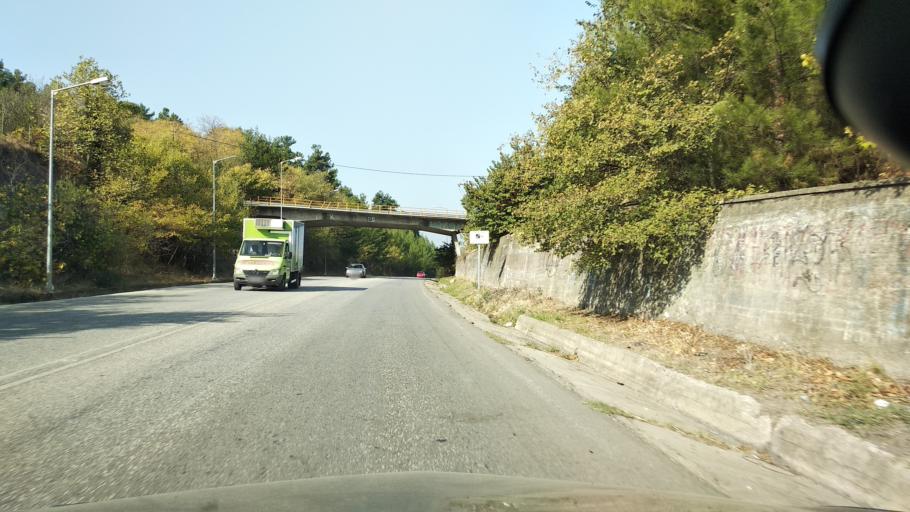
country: GR
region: Thessaly
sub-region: Trikala
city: Trikala
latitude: 39.5680
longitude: 21.7671
